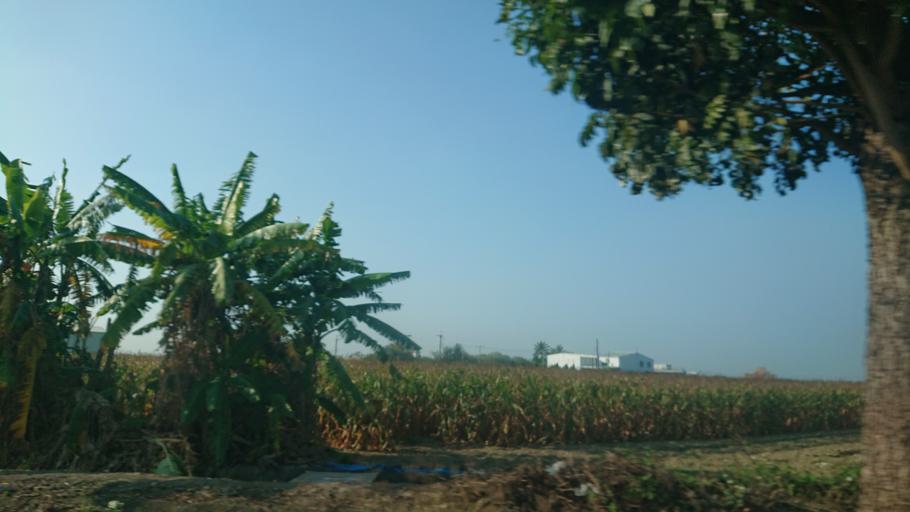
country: TW
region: Taiwan
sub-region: Tainan
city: Tainan
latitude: 23.1228
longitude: 120.2222
